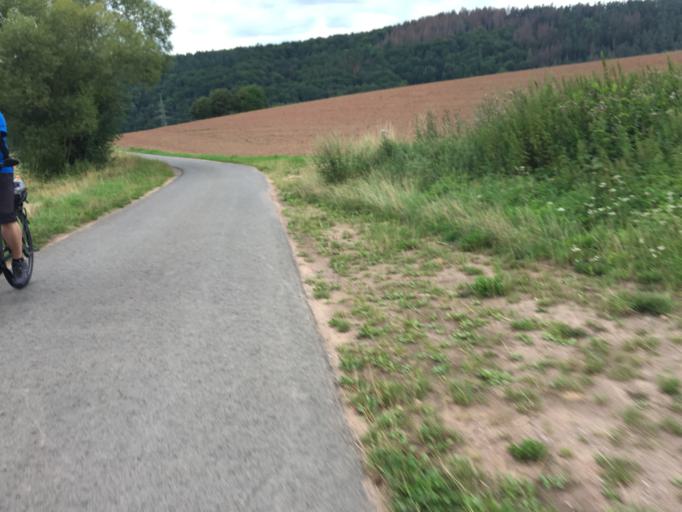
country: DE
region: Hesse
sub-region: Regierungsbezirk Kassel
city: Bad Hersfeld
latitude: 50.8873
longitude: 9.7391
